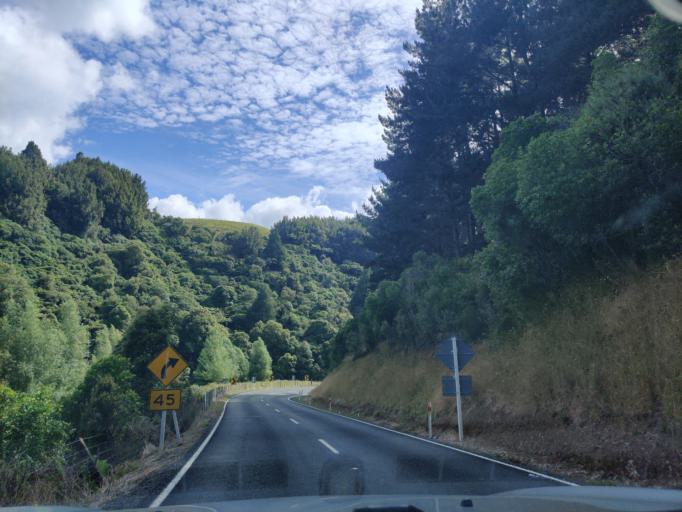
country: NZ
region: Waikato
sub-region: Otorohanga District
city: Otorohanga
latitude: -38.0974
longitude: 175.1289
